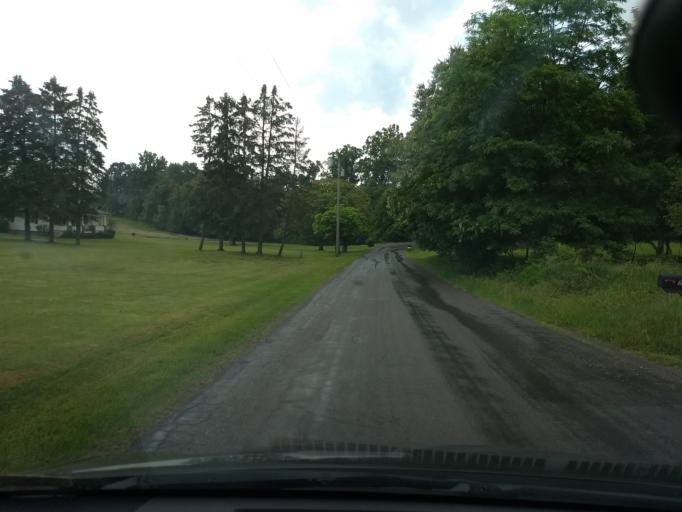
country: US
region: Pennsylvania
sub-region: Armstrong County
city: Orchard Hills
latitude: 40.5534
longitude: -79.5026
